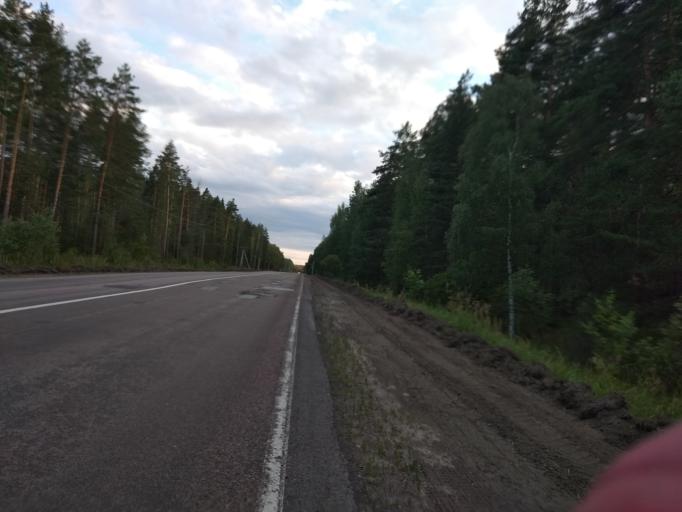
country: RU
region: Moskovskaya
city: Misheronskiy
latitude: 55.6391
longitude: 39.7516
